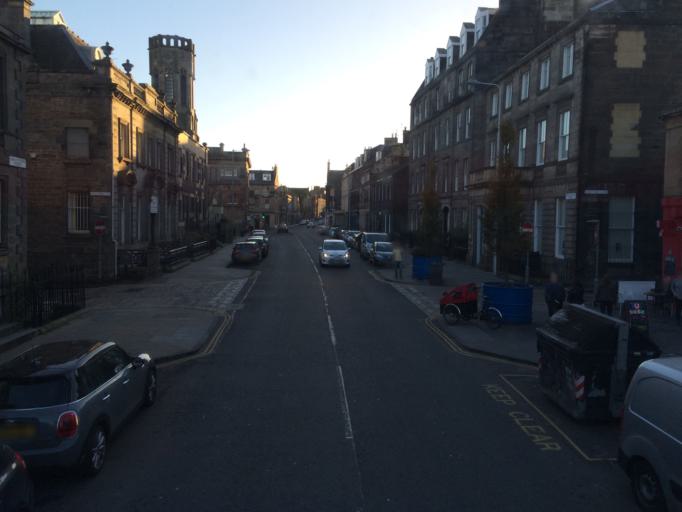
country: GB
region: Scotland
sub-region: West Lothian
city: Seafield
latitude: 55.9747
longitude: -3.1671
